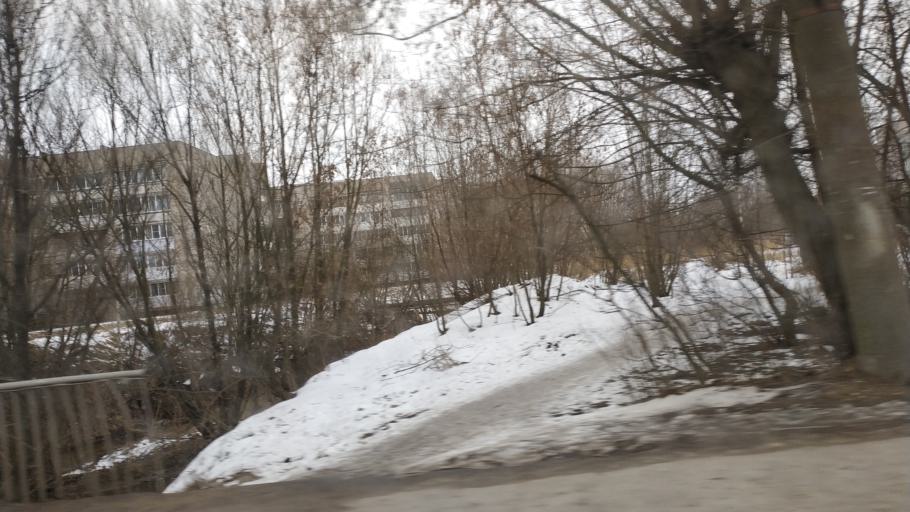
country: RU
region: Tverskaya
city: Tver
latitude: 56.8829
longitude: 35.9008
